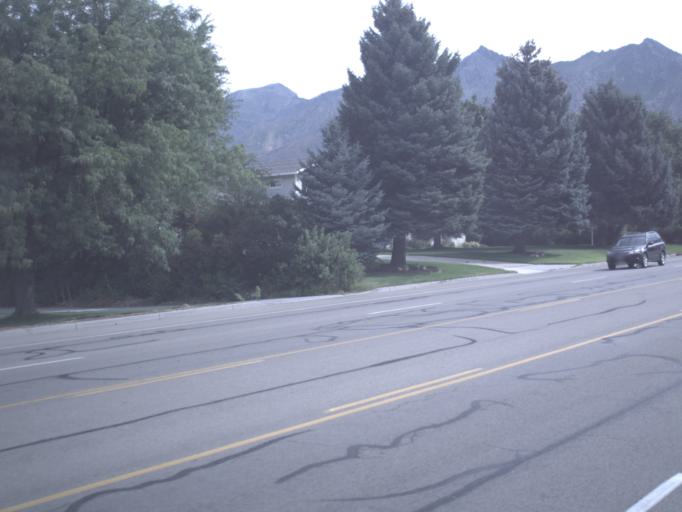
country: US
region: Utah
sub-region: Utah County
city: Alpine
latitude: 40.4319
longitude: -111.7828
